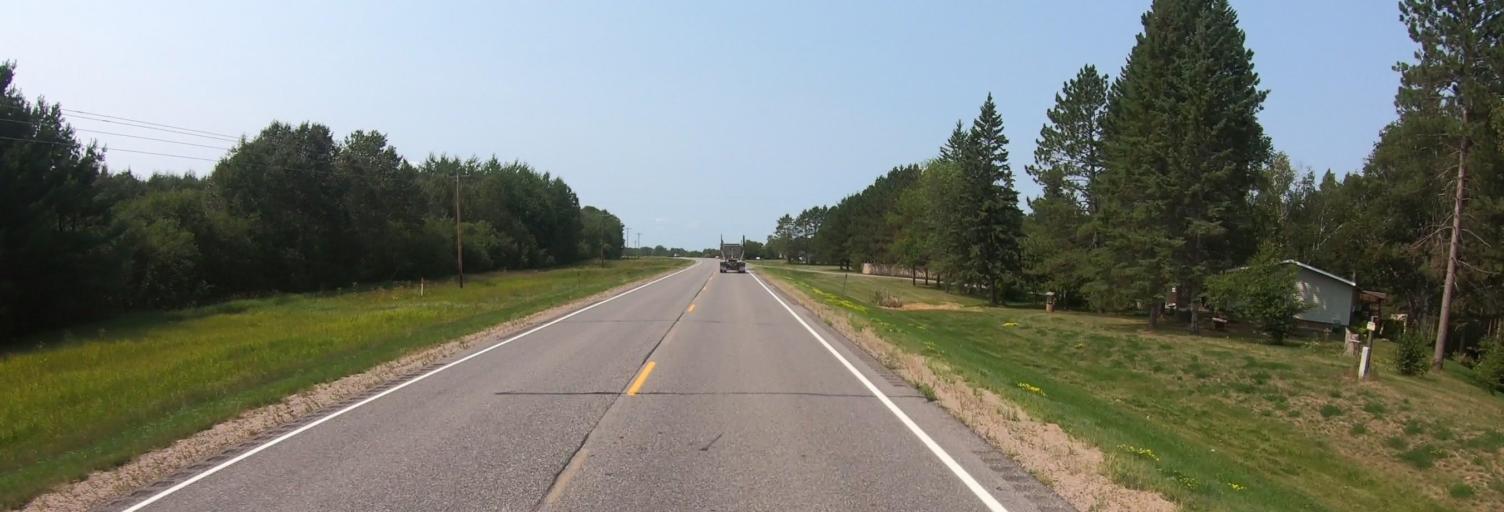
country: US
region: Minnesota
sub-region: Koochiching County
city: International Falls
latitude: 48.5187
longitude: -93.6272
